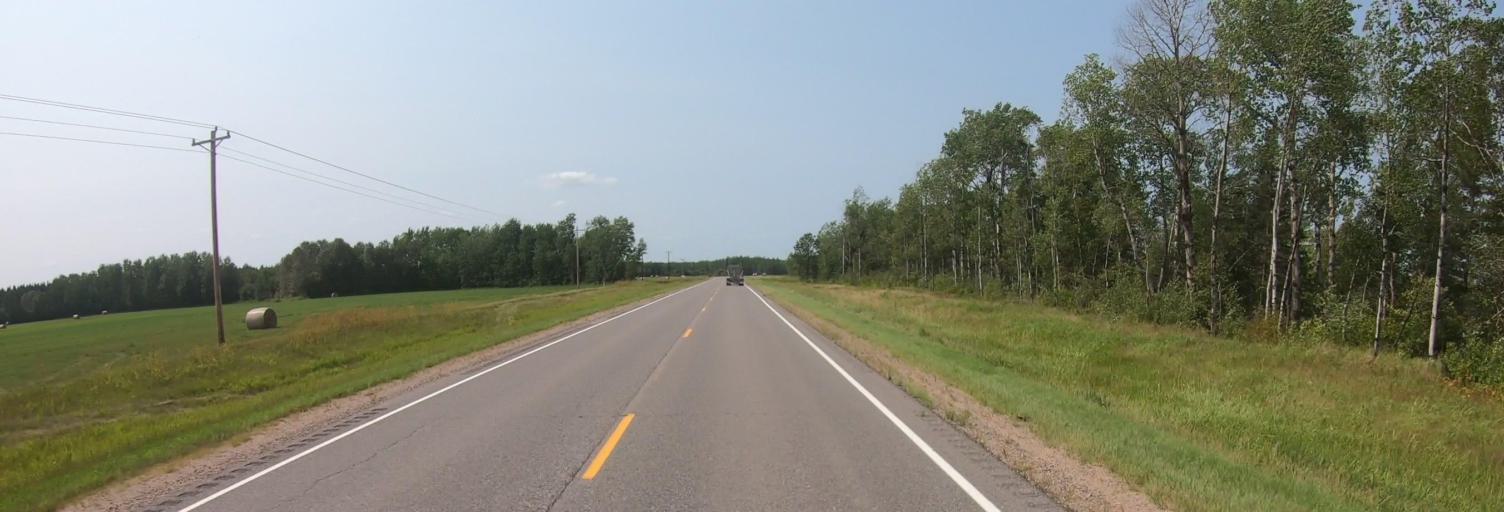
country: US
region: Minnesota
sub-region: Koochiching County
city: International Falls
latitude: 48.5159
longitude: -93.6489
